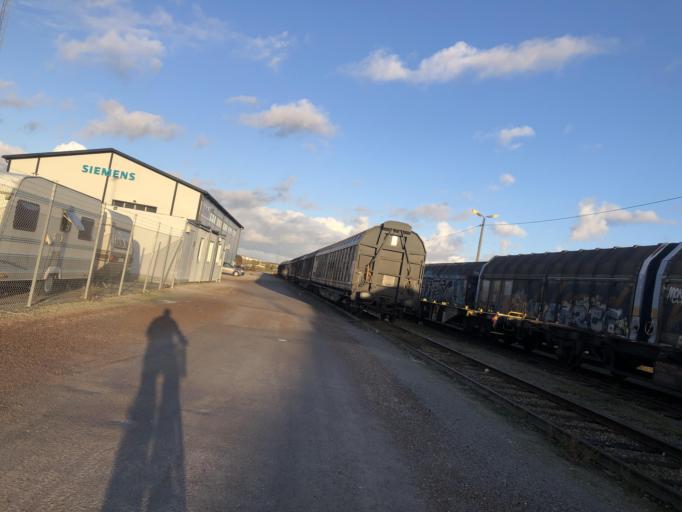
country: SE
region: Skane
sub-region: Malmo
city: Malmoe
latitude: 55.6132
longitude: 13.0228
